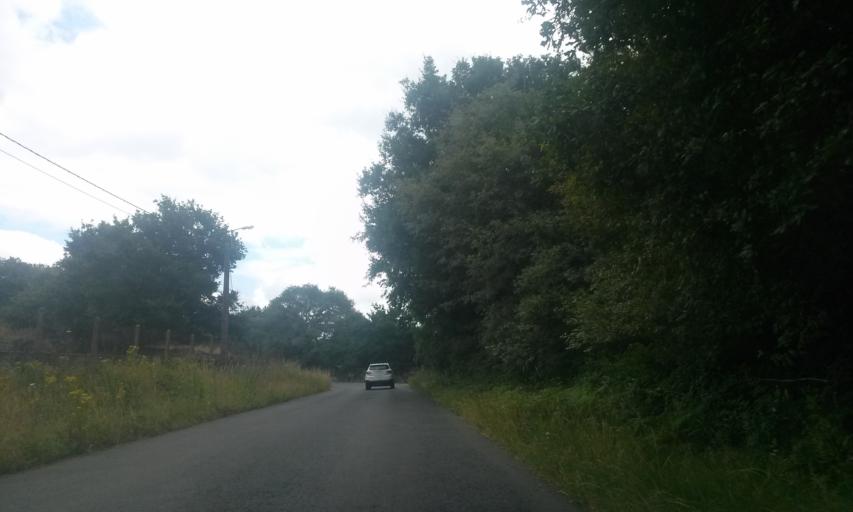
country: ES
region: Galicia
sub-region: Provincia de Lugo
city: Outeiro de Rei
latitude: 43.0653
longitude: -7.6228
